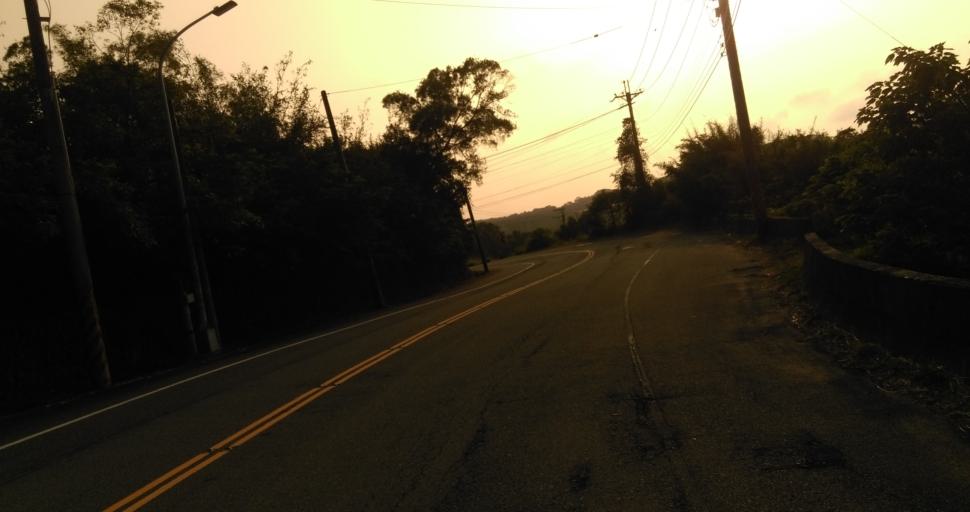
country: TW
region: Taiwan
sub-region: Hsinchu
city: Hsinchu
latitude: 24.7570
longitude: 120.9434
